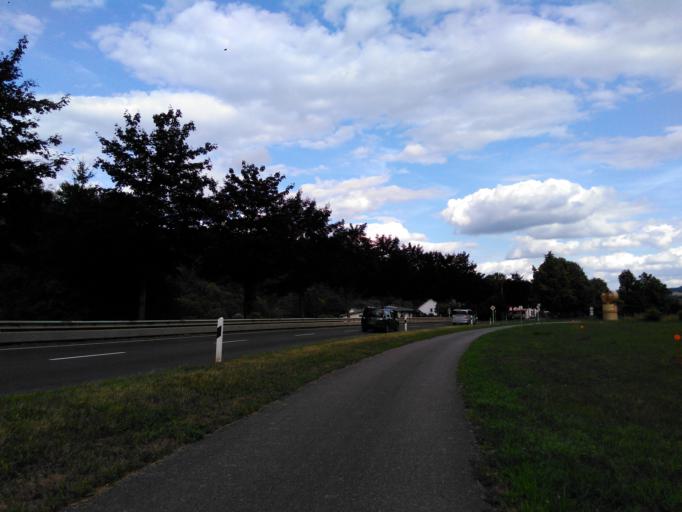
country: DE
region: Rheinland-Pfalz
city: Minden
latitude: 49.8213
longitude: 6.4704
